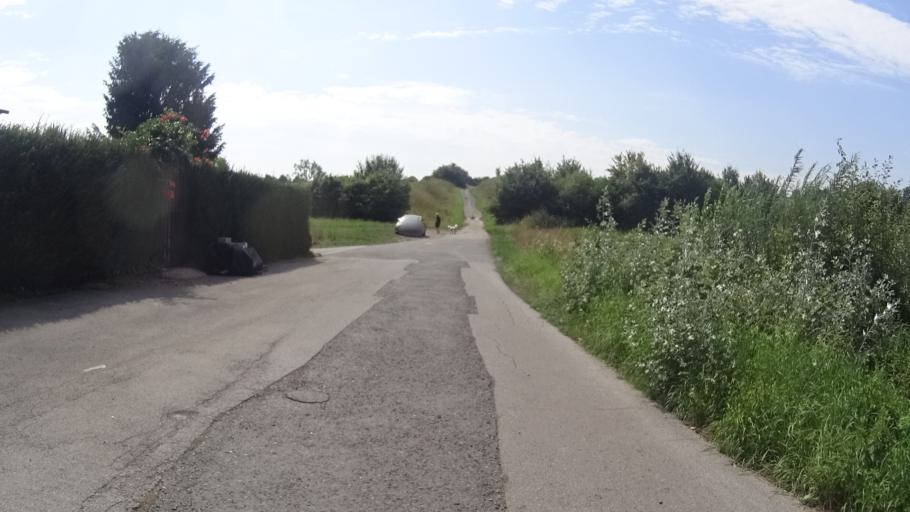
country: DE
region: North Rhine-Westphalia
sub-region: Regierungsbezirk Arnsberg
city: Dortmund
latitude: 51.4788
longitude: 7.4165
